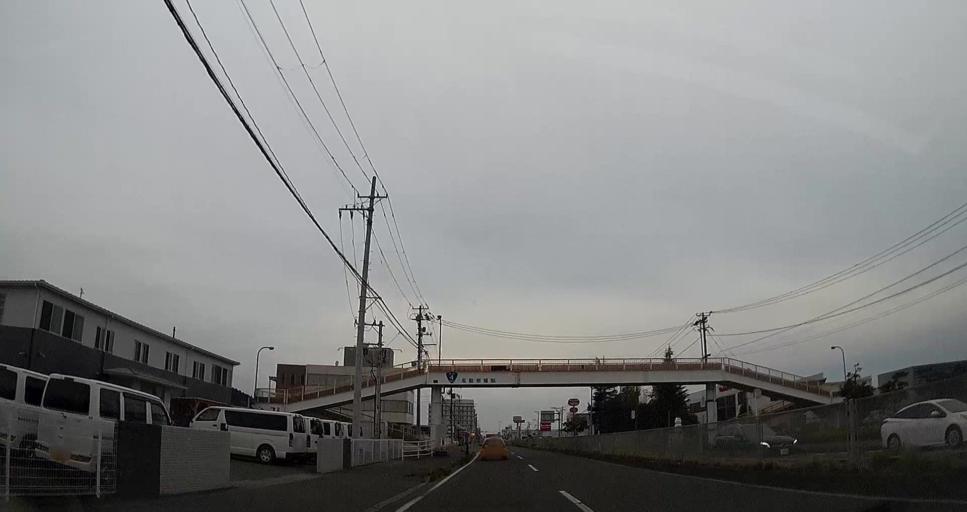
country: JP
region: Miyagi
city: Iwanuma
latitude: 38.1448
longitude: 140.8818
